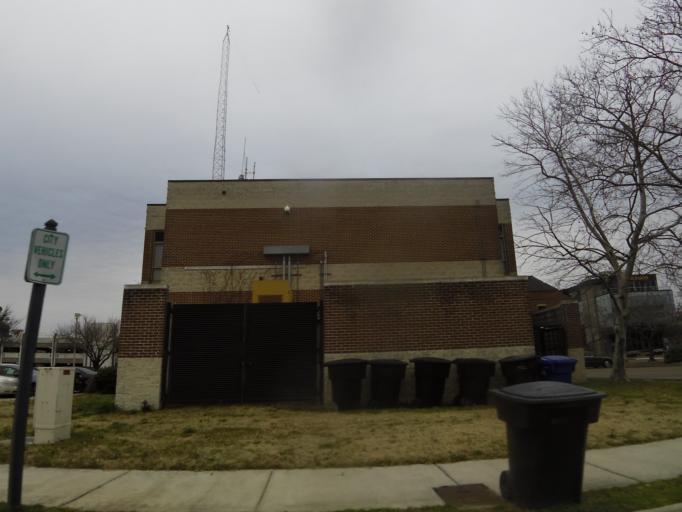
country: US
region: Virginia
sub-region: City of Portsmouth
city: Portsmouth
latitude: 36.8331
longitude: -76.2990
